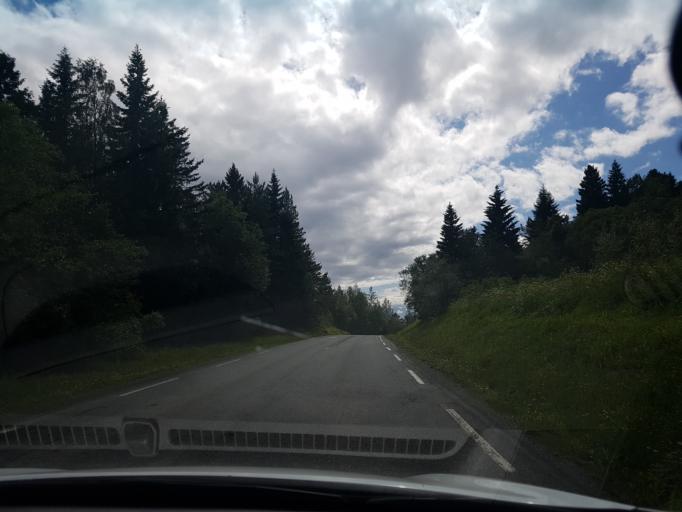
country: NO
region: Nord-Trondelag
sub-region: Stjordal
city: Stjordal
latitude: 63.6141
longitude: 10.9067
